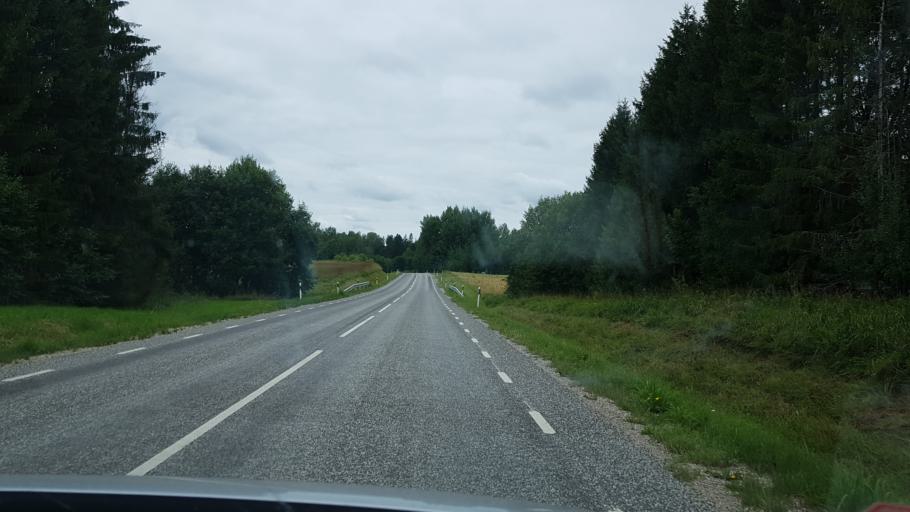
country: EE
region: Vorumaa
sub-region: Antsla vald
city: Vana-Antsla
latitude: 58.0045
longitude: 26.6378
